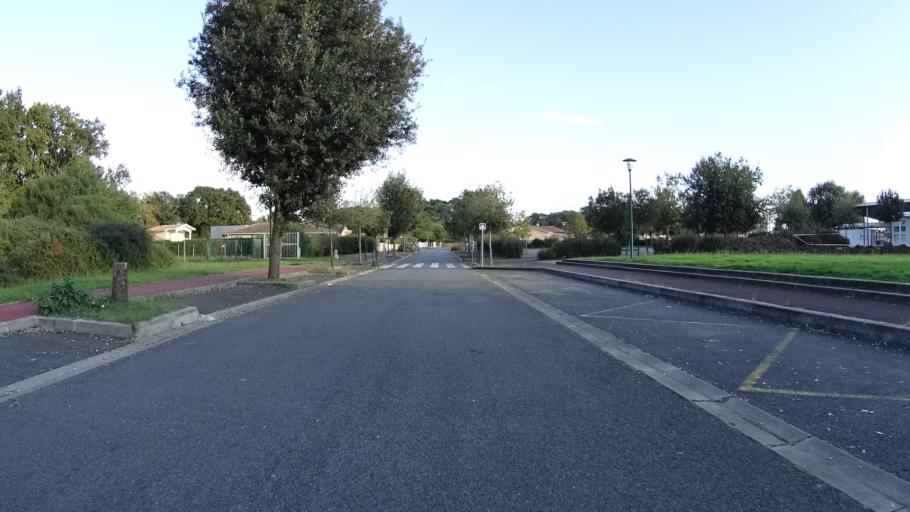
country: FR
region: Aquitaine
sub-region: Departement des Landes
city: Saint-Paul-les-Dax
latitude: 43.7365
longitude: -1.0475
